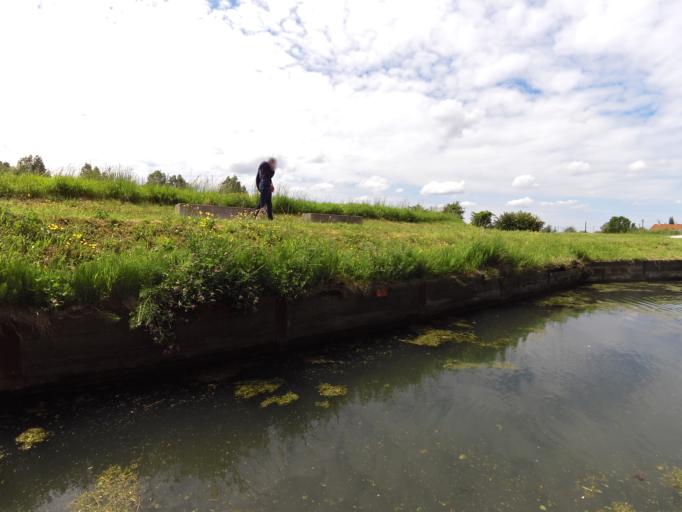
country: FR
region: Nord-Pas-de-Calais
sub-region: Departement du Pas-de-Calais
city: Saint-Martin-au-Laert
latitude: 50.7591
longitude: 2.2463
